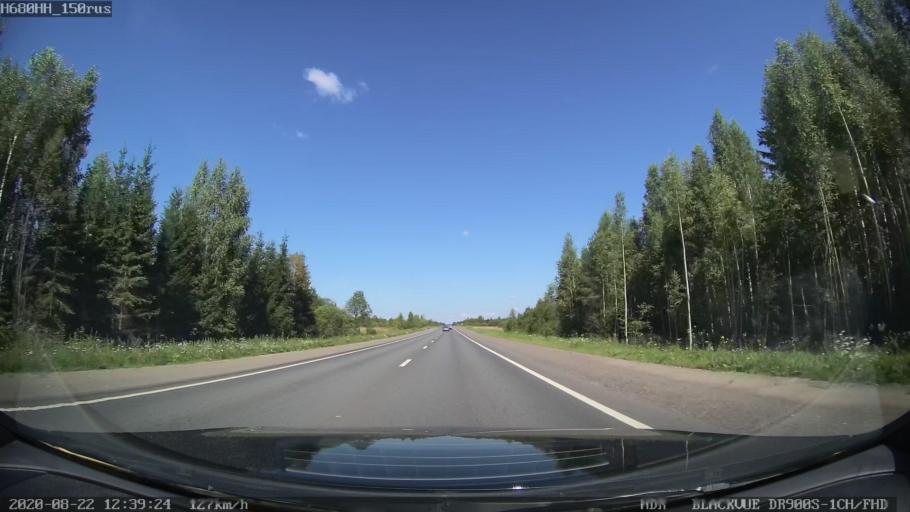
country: RU
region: Tverskaya
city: Rameshki
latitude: 57.3301
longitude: 36.0934
